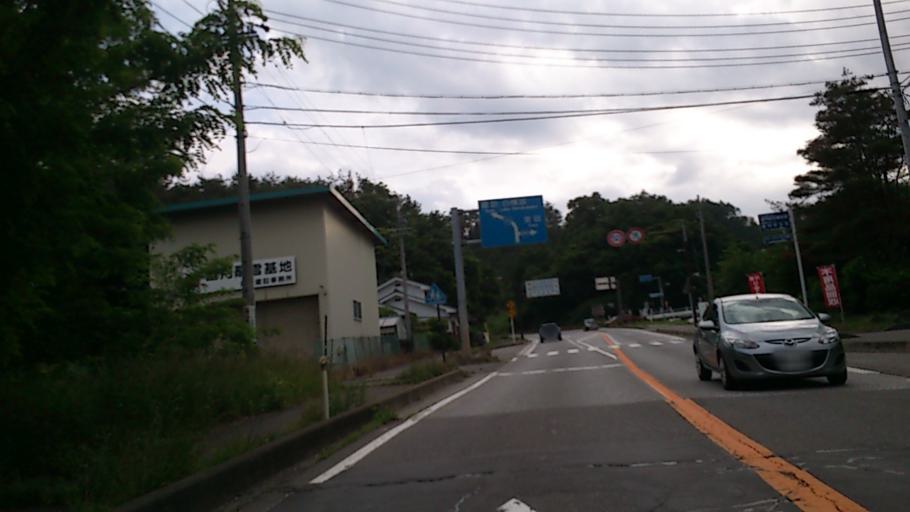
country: JP
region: Nagano
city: Komoro
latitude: 36.2671
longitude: 138.3746
